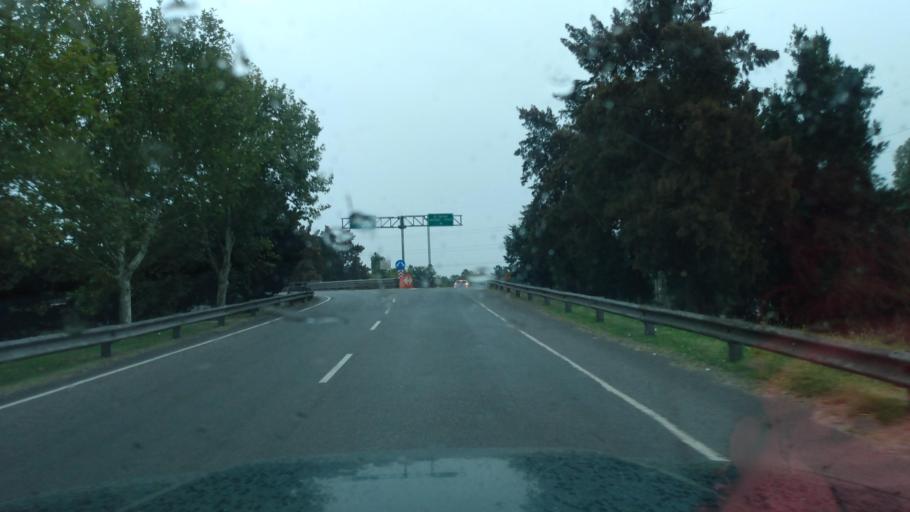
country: AR
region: Buenos Aires
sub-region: Partido de San Isidro
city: San Isidro
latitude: -34.4941
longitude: -58.5559
